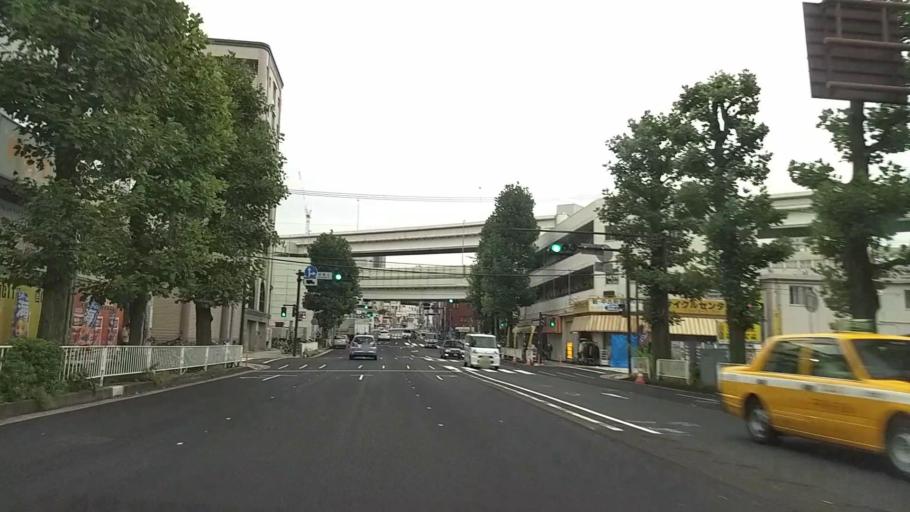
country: JP
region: Kanagawa
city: Yokohama
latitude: 35.4374
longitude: 139.6369
